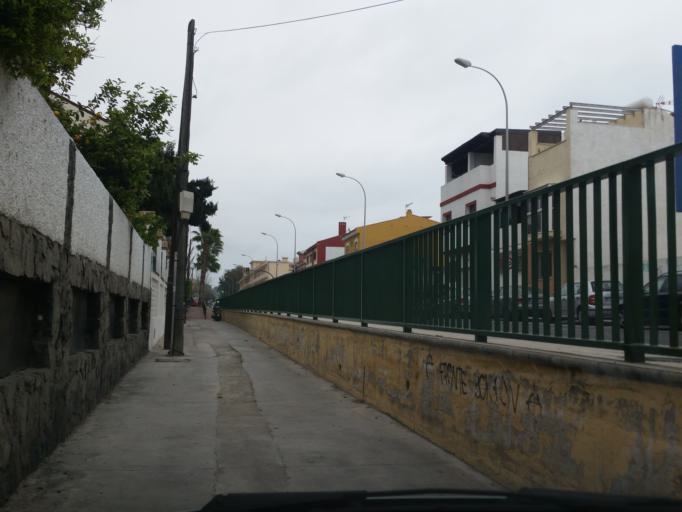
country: ES
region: Andalusia
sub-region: Provincia de Malaga
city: Malaga
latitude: 36.7200
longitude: -4.3678
